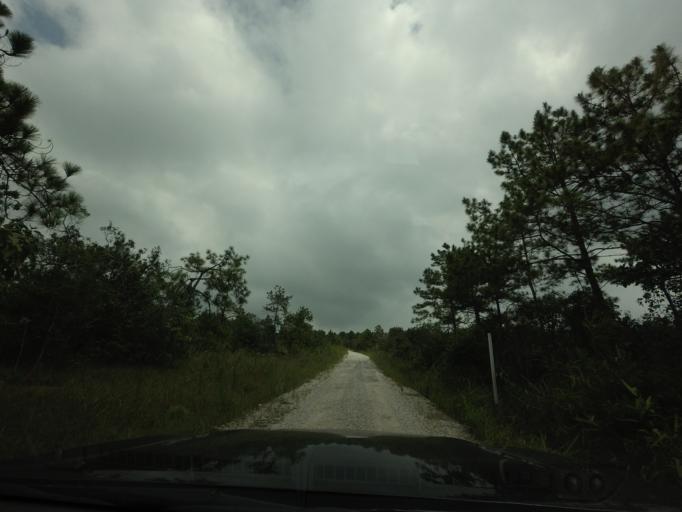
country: TH
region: Loei
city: Phu Ruea
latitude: 17.5024
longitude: 101.3398
